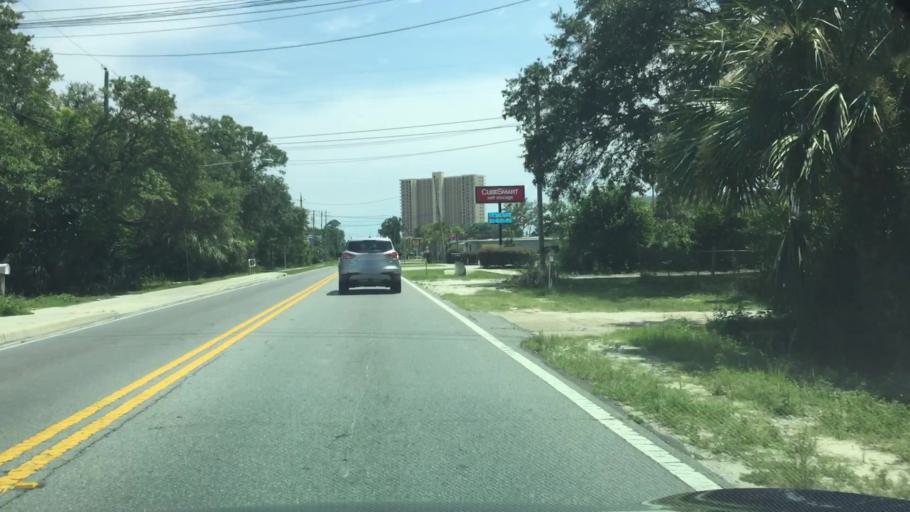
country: US
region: Florida
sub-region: Bay County
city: Panama City Beach
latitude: 30.1746
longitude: -85.7898
